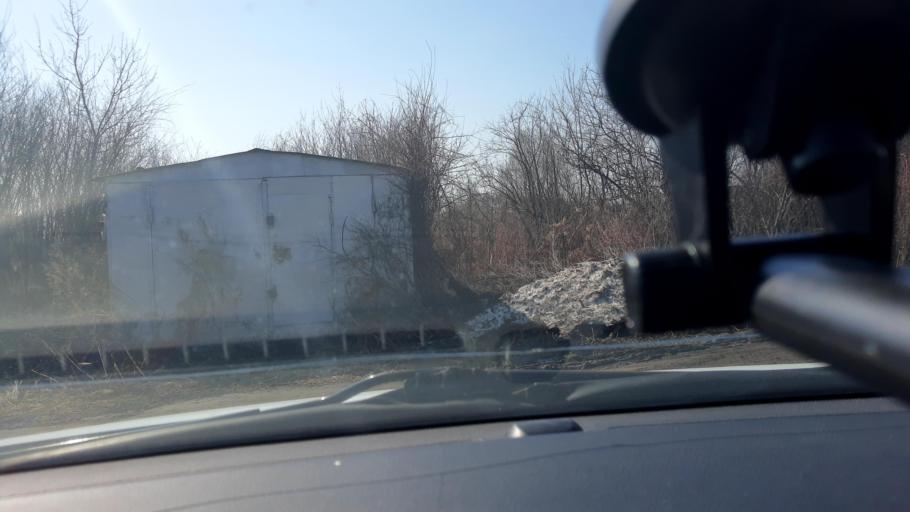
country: RU
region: Bashkortostan
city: Mikhaylovka
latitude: 54.7218
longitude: 55.8274
